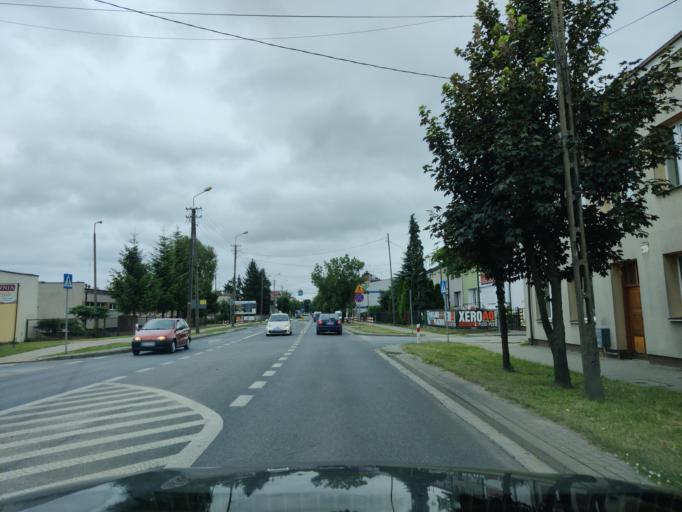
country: PL
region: Masovian Voivodeship
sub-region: Powiat pultuski
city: Pultusk
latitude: 52.7121
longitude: 21.0836
